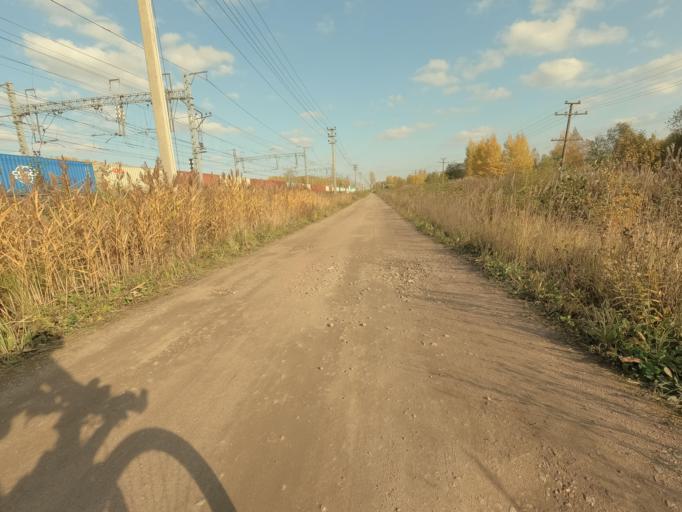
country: RU
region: Leningrad
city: Mga
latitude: 59.7567
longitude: 31.1059
